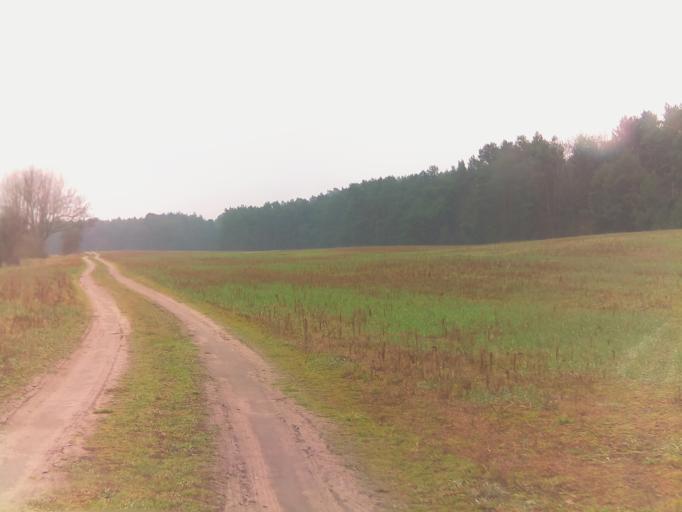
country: DE
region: Brandenburg
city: Lieberose
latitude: 52.0118
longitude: 14.2170
